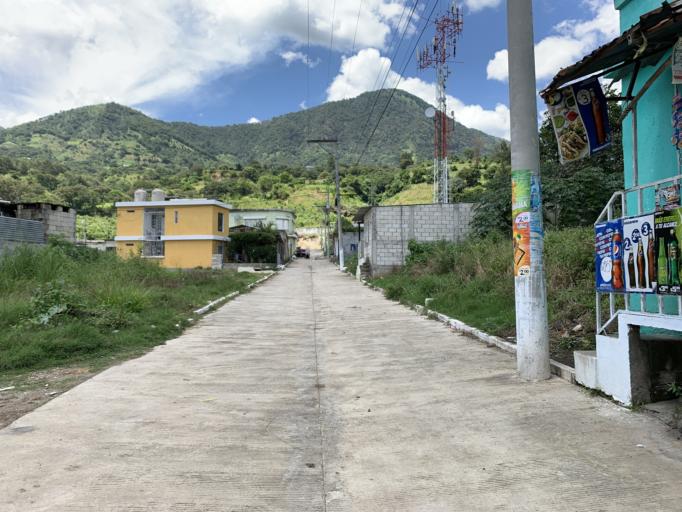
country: GT
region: Guatemala
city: Amatitlan
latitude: 14.4888
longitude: -90.6435
